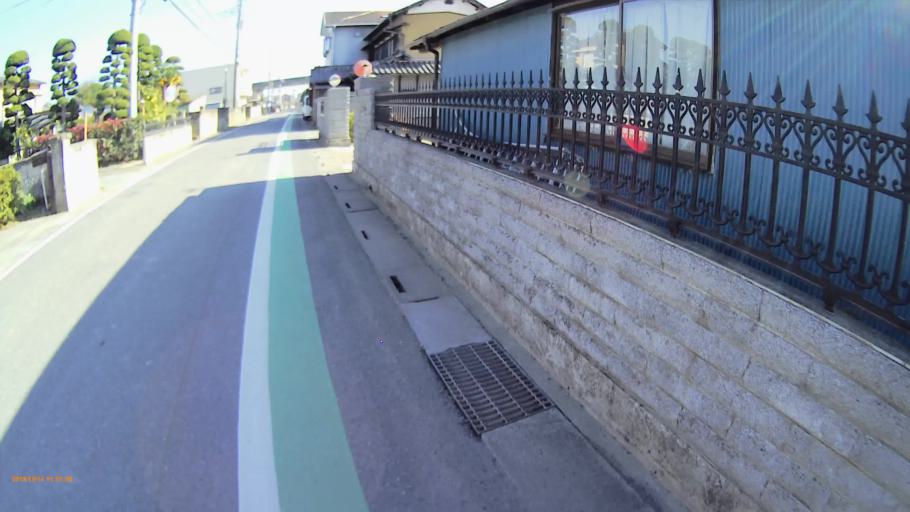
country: JP
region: Saitama
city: Kumagaya
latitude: 36.1224
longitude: 139.4097
